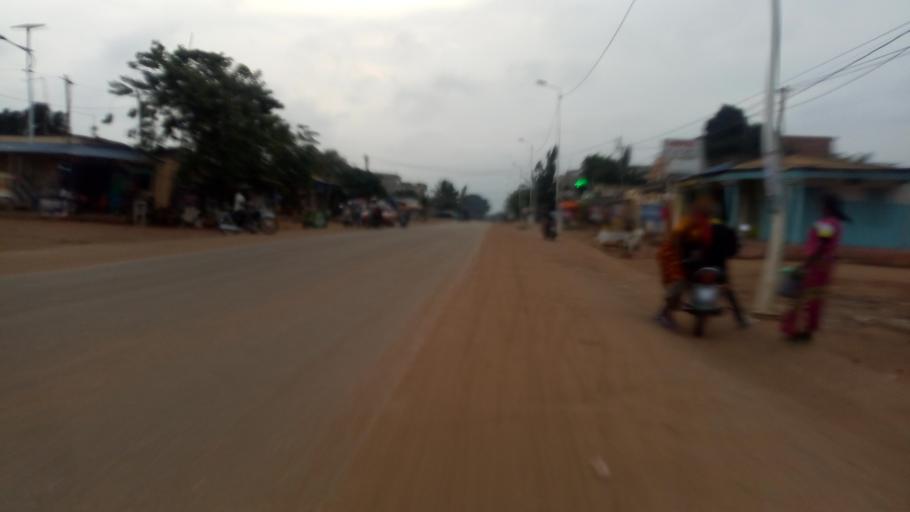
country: TG
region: Maritime
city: Lome
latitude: 6.1811
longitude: 1.1913
